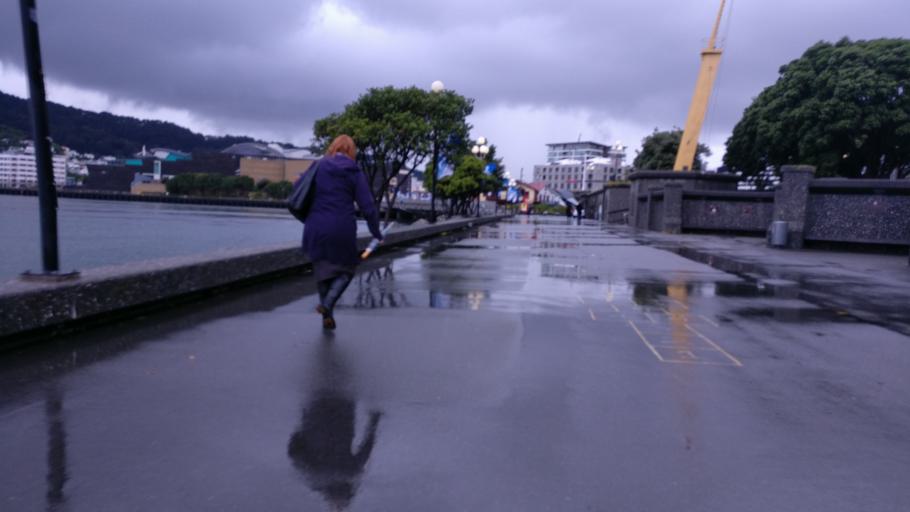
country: NZ
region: Wellington
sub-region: Wellington City
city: Wellington
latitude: -41.2867
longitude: 174.7791
